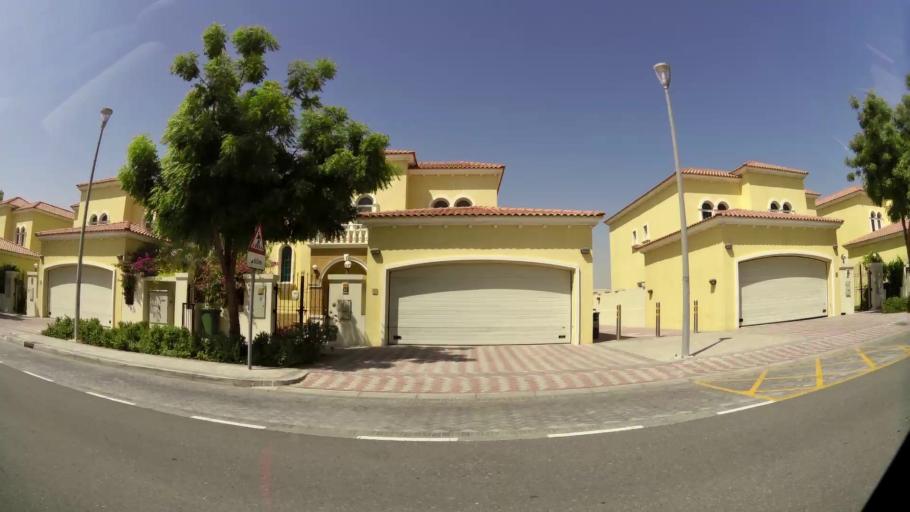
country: AE
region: Dubai
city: Dubai
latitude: 25.0476
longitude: 55.1581
